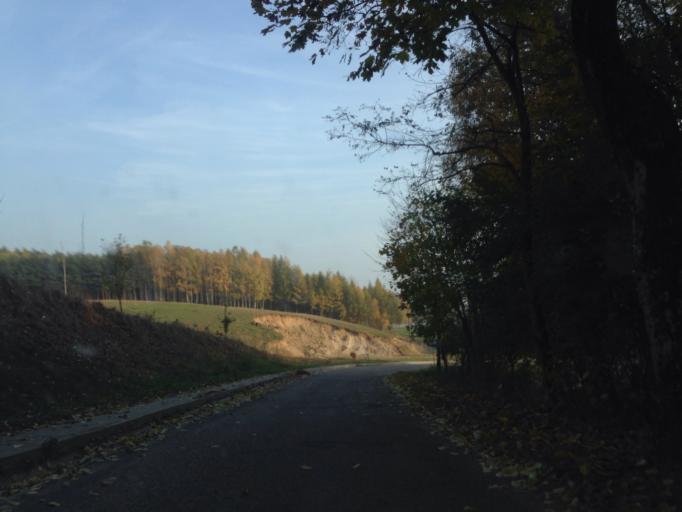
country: PL
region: Kujawsko-Pomorskie
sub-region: Powiat brodnicki
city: Brzozie
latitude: 53.2873
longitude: 19.6933
